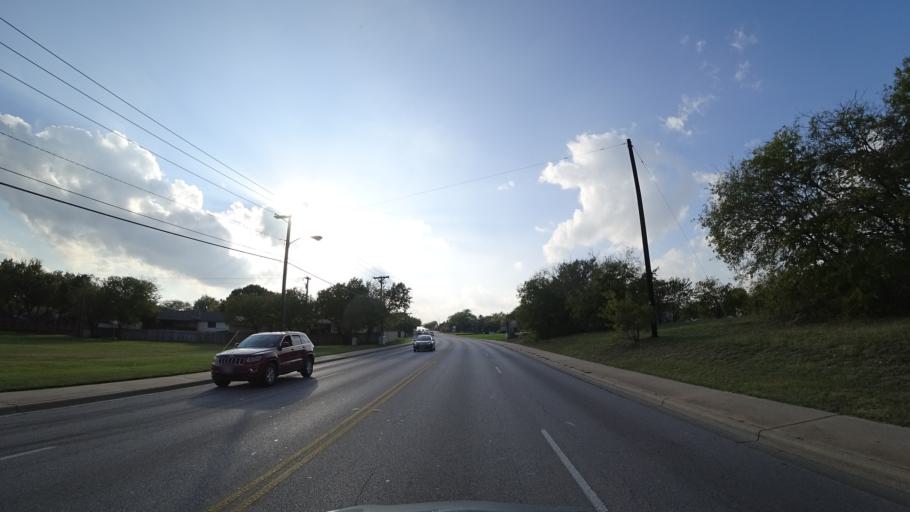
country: US
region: Texas
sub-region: Williamson County
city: Round Rock
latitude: 30.4960
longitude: -97.6667
